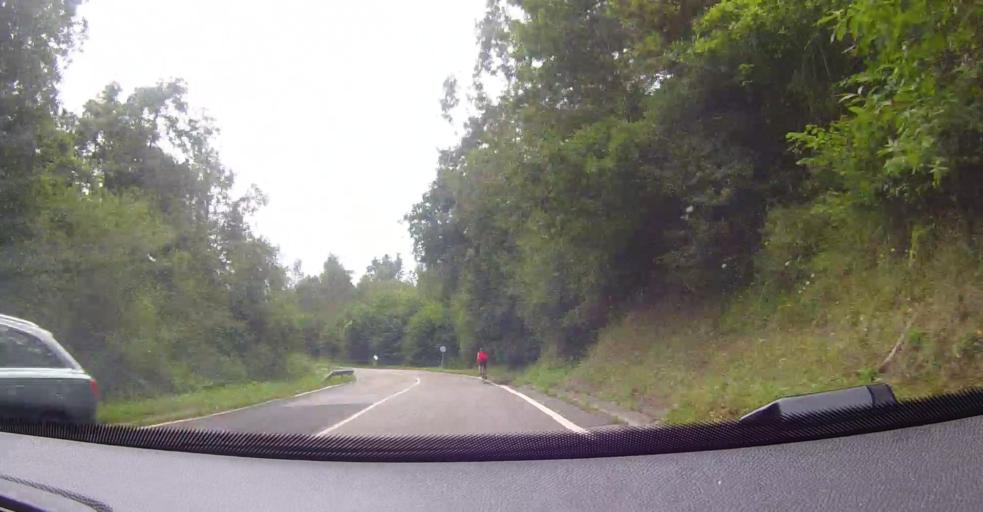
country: ES
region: Basque Country
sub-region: Bizkaia
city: Balmaseda
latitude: 43.2418
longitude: -3.2880
